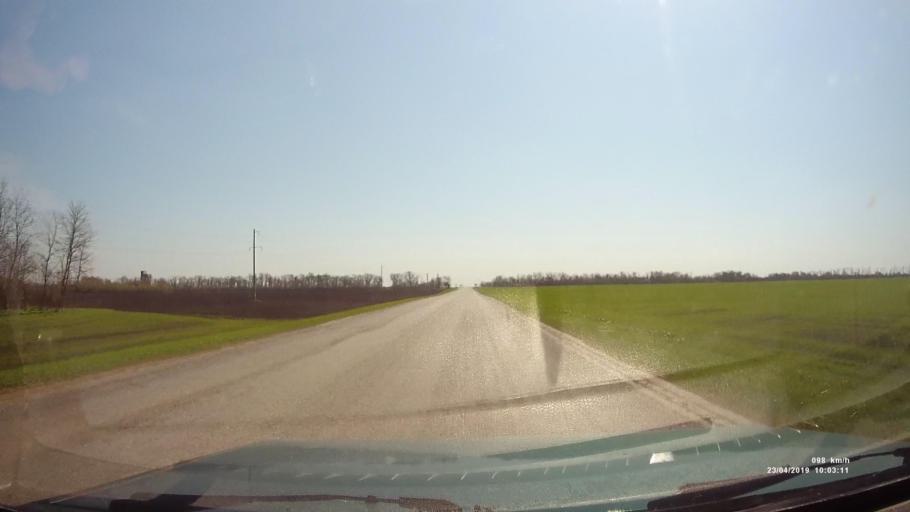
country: RU
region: Rostov
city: Sovetskoye
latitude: 46.7568
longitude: 42.1836
